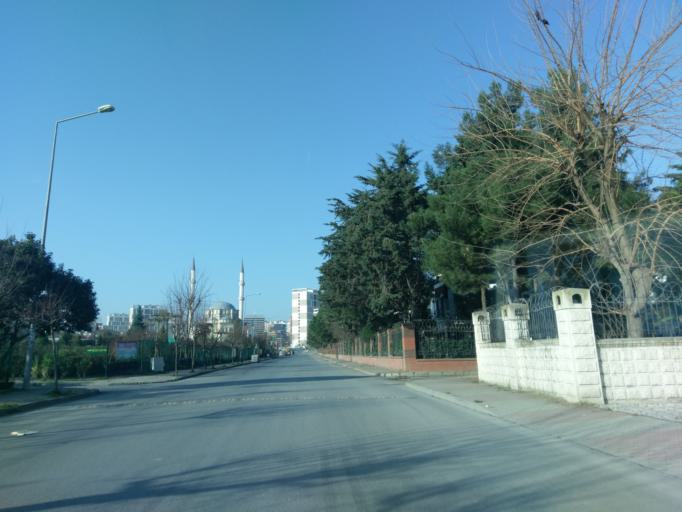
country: TR
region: Istanbul
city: Mahmutbey
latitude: 41.0325
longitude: 28.7659
